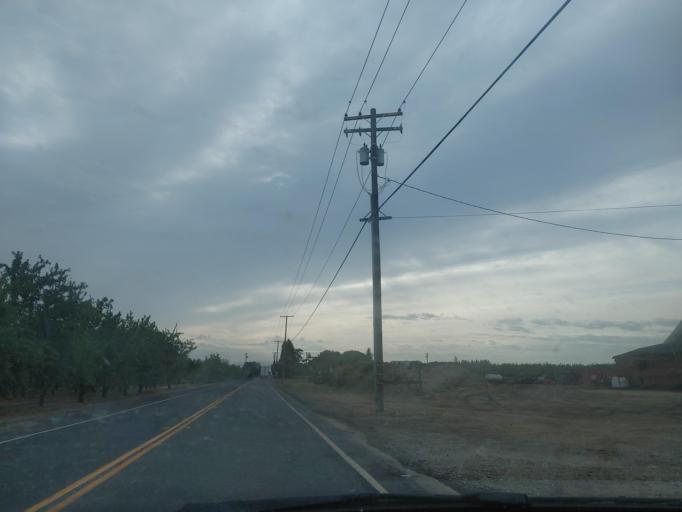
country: US
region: California
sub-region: Stanislaus County
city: Salida
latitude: 37.6816
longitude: -121.1080
